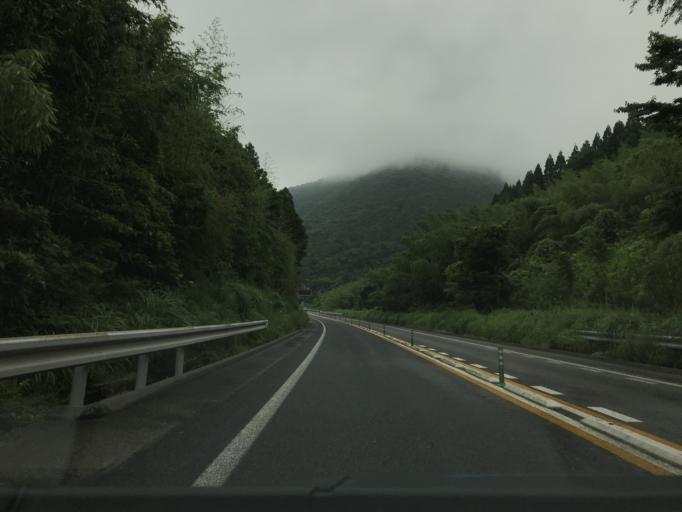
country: JP
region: Oita
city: Bungo-Takada-shi
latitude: 33.4918
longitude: 131.3213
